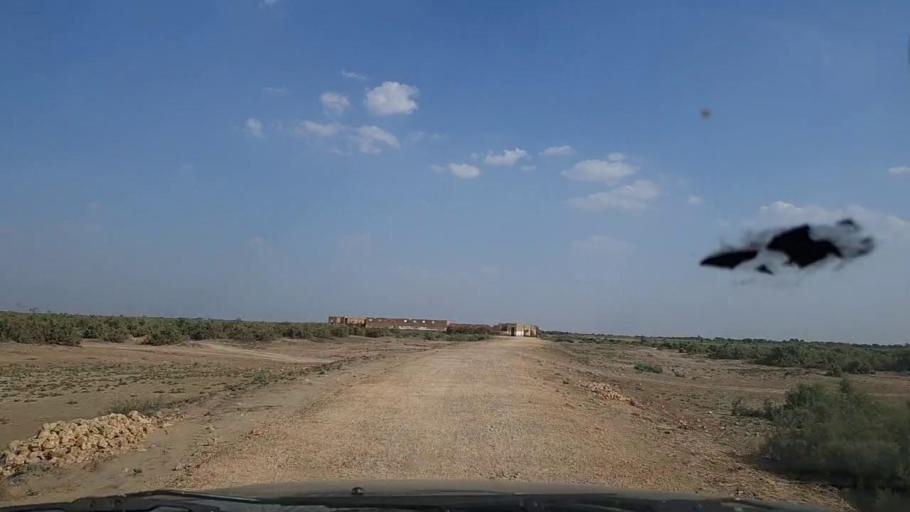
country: PK
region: Sindh
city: Daro Mehar
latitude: 24.7870
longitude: 68.0780
